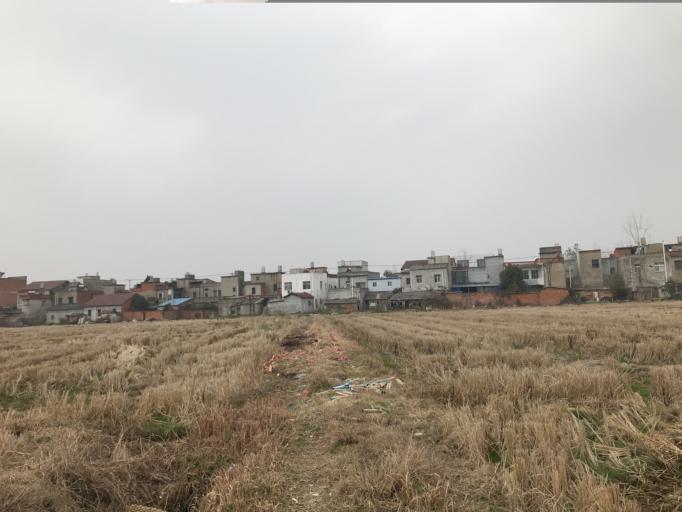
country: CN
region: Hubei
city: Shihe
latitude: 30.7629
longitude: 113.0906
